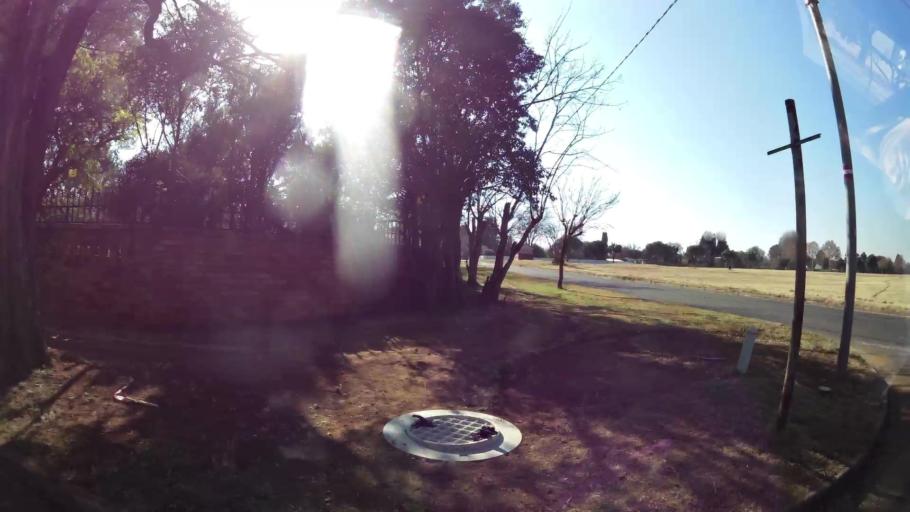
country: ZA
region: Gauteng
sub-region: Ekurhuleni Metropolitan Municipality
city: Benoni
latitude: -26.1547
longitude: 28.3266
